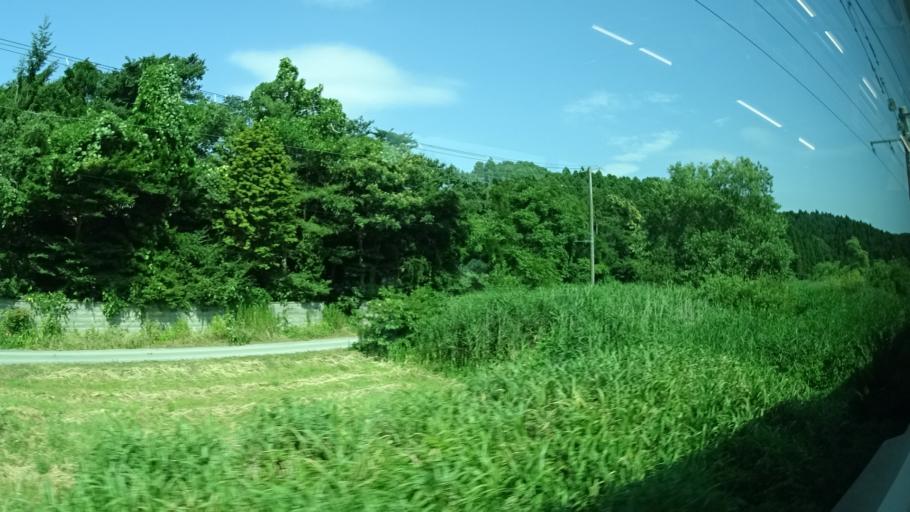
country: JP
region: Miyagi
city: Kogota
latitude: 38.4980
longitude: 141.0860
